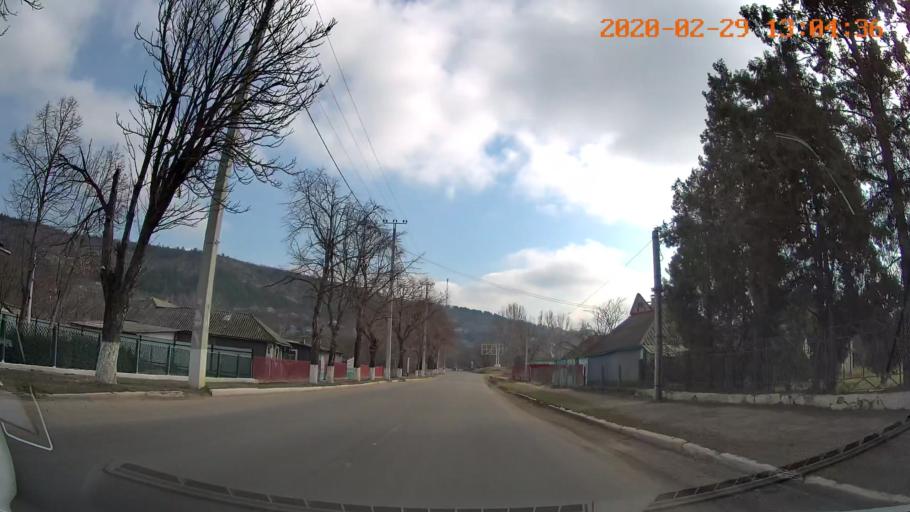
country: MD
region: Telenesti
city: Camenca
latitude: 48.0257
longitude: 28.7054
